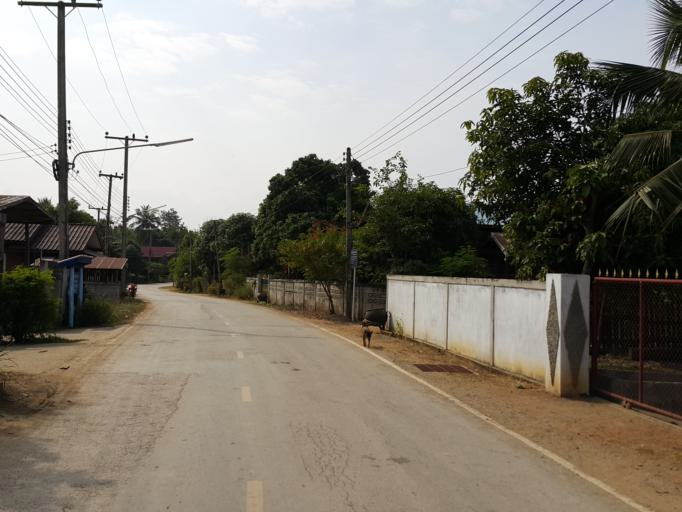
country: TH
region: Sukhothai
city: Thung Saliam
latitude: 17.3240
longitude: 99.4499
